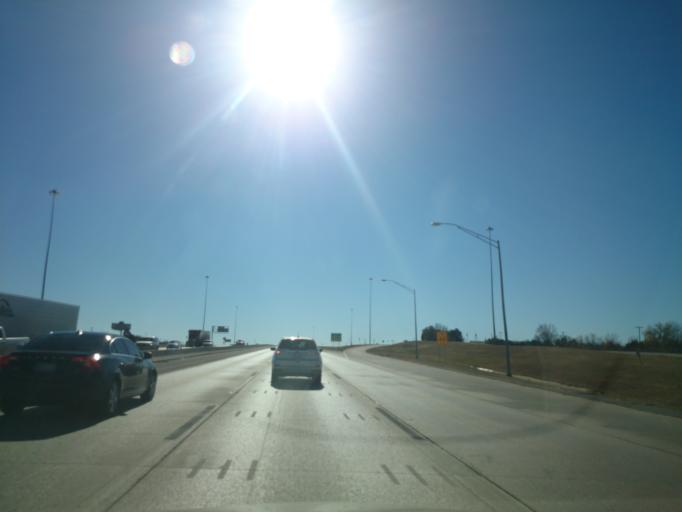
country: US
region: Oklahoma
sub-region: Oklahoma County
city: Edmond
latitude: 35.6150
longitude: -97.4251
